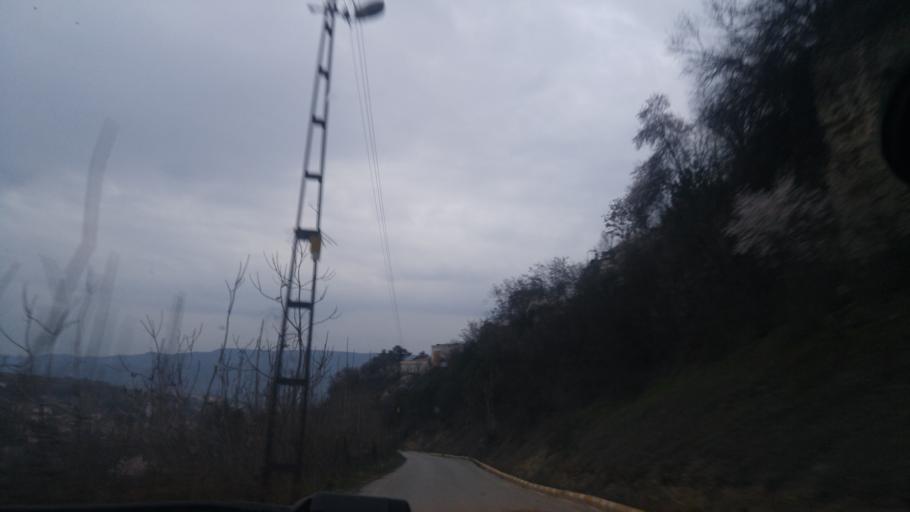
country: TR
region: Karabuk
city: Safranbolu
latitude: 41.2553
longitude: 32.6840
